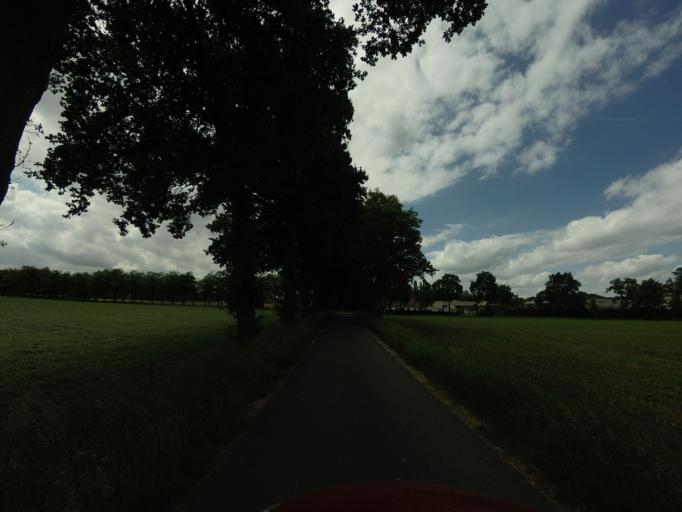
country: BE
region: Flanders
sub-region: Provincie Oost-Vlaanderen
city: Knesselare
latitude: 51.1613
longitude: 3.4326
